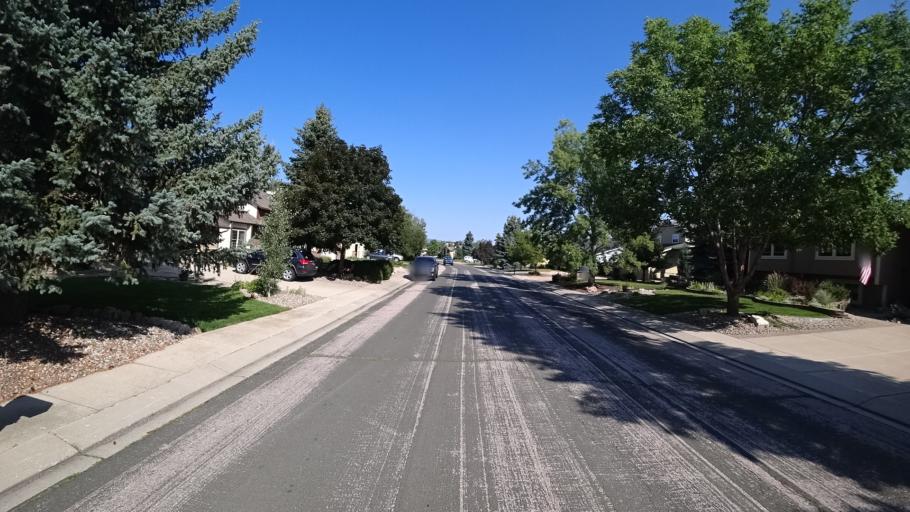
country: US
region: Colorado
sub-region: El Paso County
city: Air Force Academy
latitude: 38.9572
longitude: -104.7805
